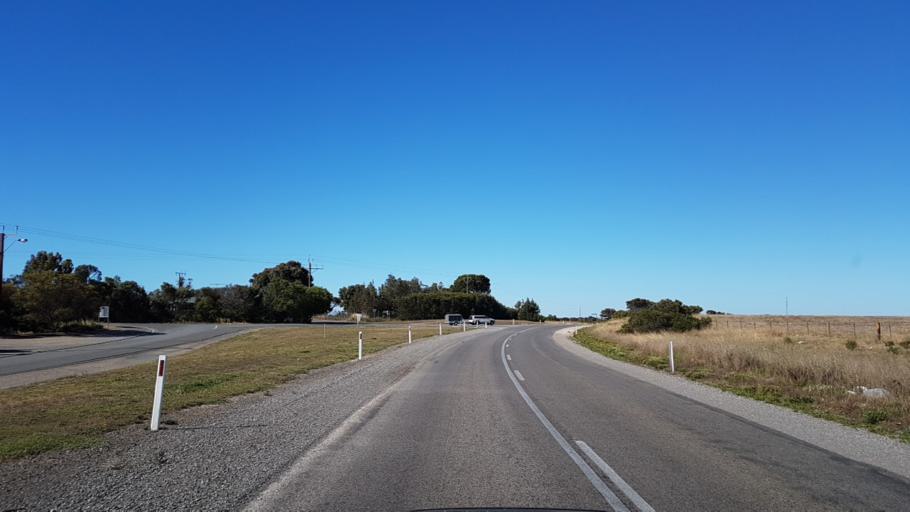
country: AU
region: South Australia
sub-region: Yorke Peninsula
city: Honiton
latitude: -34.8921
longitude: 137.4607
